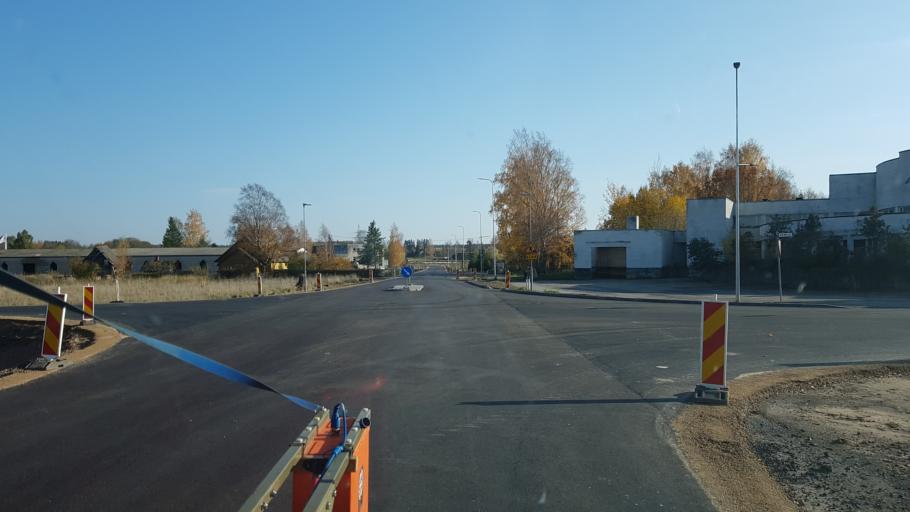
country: EE
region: Vorumaa
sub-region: Antsla vald
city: Vana-Antsla
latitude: 57.8422
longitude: 26.4775
